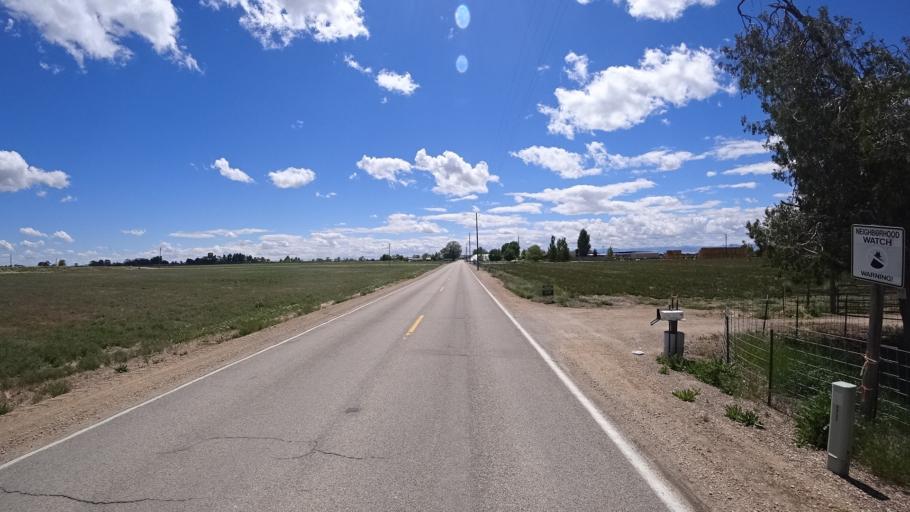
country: US
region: Idaho
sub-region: Ada County
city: Kuna
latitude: 43.5553
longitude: -116.4537
